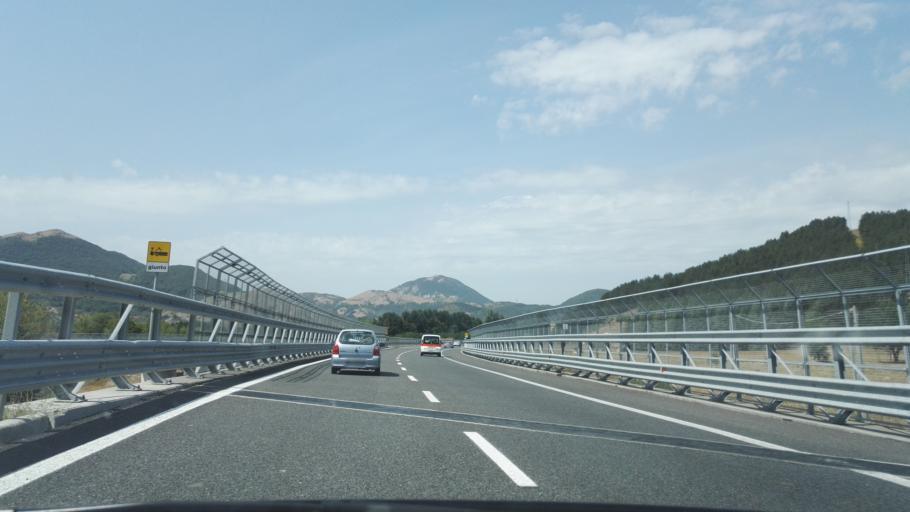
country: IT
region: Calabria
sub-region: Provincia di Cosenza
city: Morano Calabro
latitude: 39.8642
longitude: 16.0898
